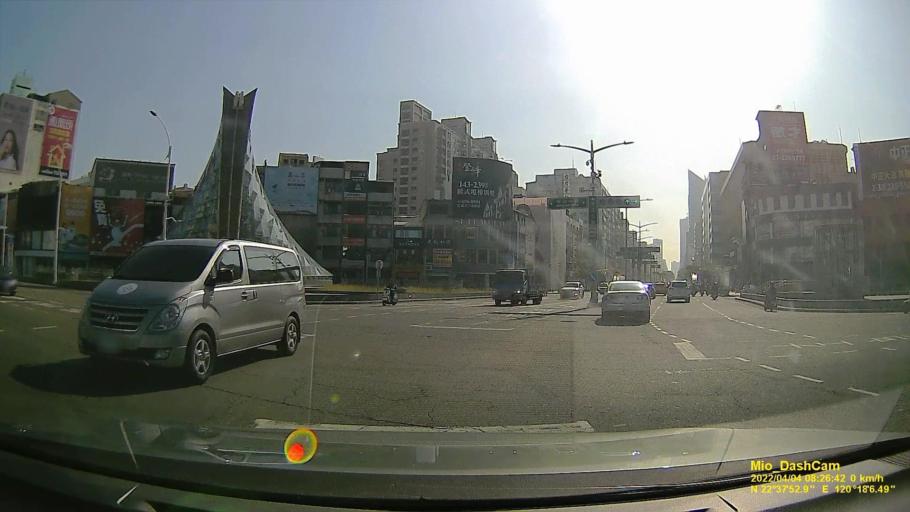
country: TW
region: Kaohsiung
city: Kaohsiung
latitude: 22.6313
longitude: 120.3017
